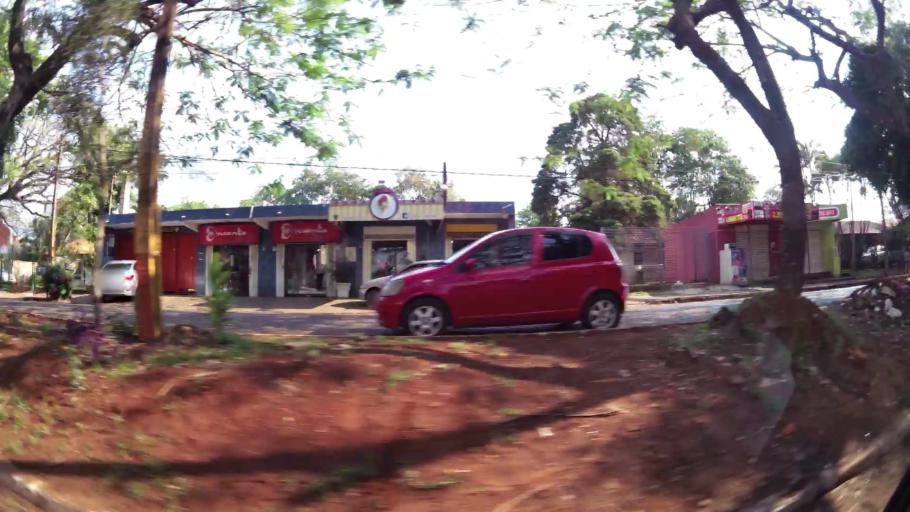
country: PY
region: Alto Parana
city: Presidente Franco
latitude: -25.5321
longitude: -54.6279
